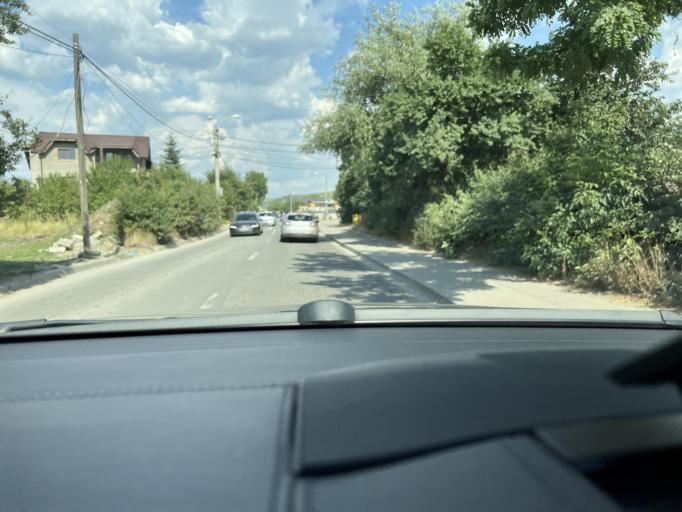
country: RO
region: Cluj
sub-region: Comuna Apahida
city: Sannicoara
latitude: 46.7793
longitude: 23.6925
